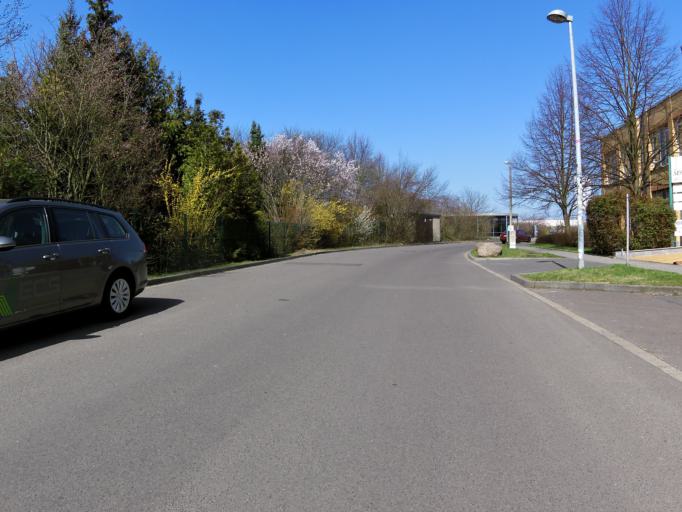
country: DE
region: Saxony
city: Leipzig
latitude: 51.3781
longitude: 12.3116
